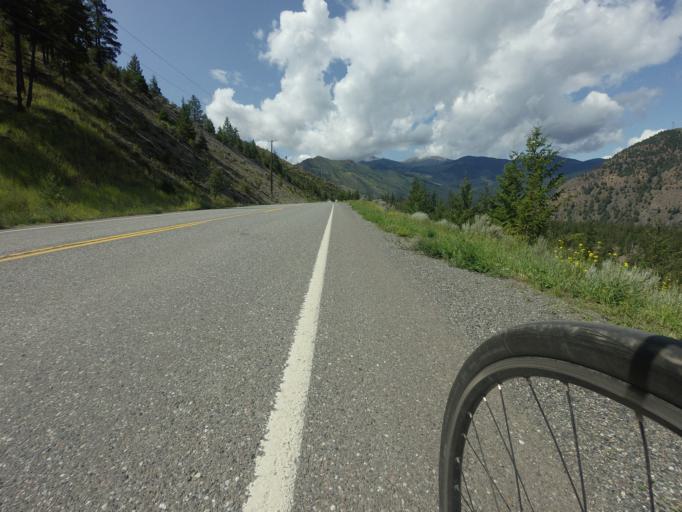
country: CA
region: British Columbia
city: Lillooet
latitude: 50.7588
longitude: -121.9129
